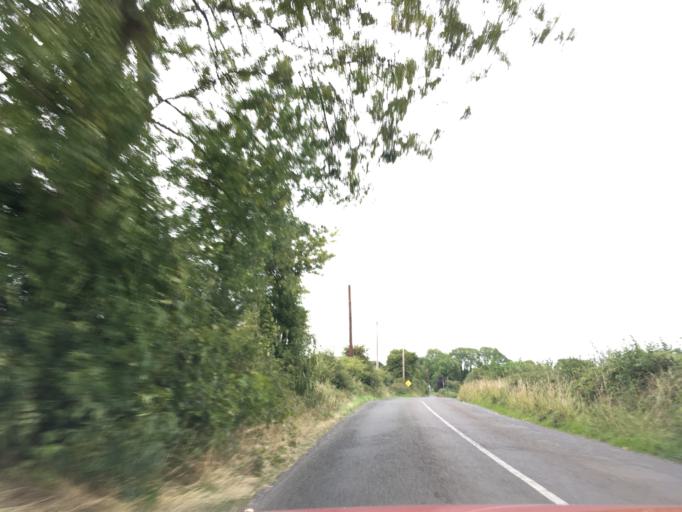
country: IE
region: Munster
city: Cashel
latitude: 52.4760
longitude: -7.8854
